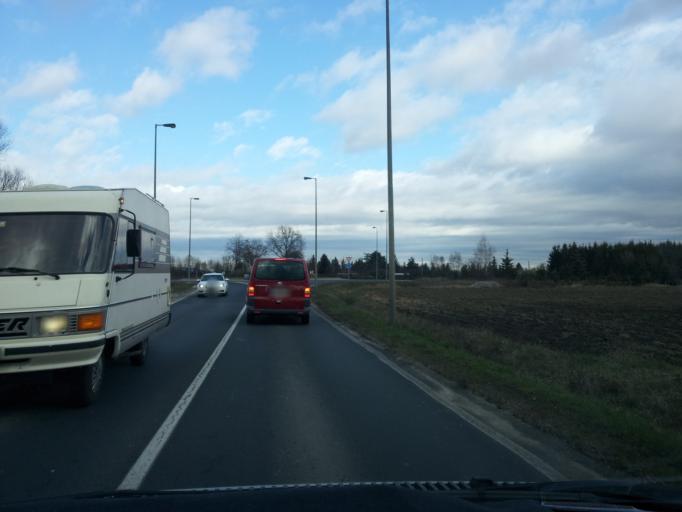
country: HU
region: Vas
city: Gencsapati
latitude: 47.2645
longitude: 16.6104
